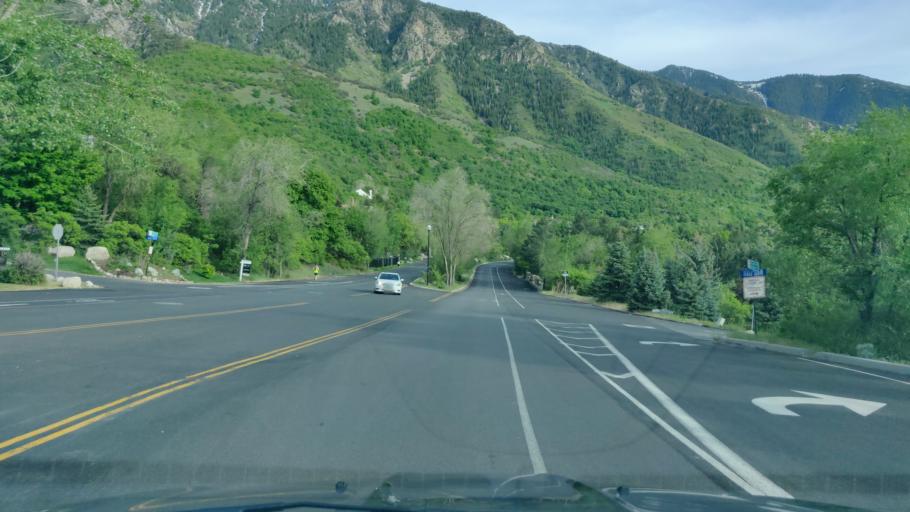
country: US
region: Utah
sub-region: Salt Lake County
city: Granite
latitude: 40.5606
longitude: -111.8011
